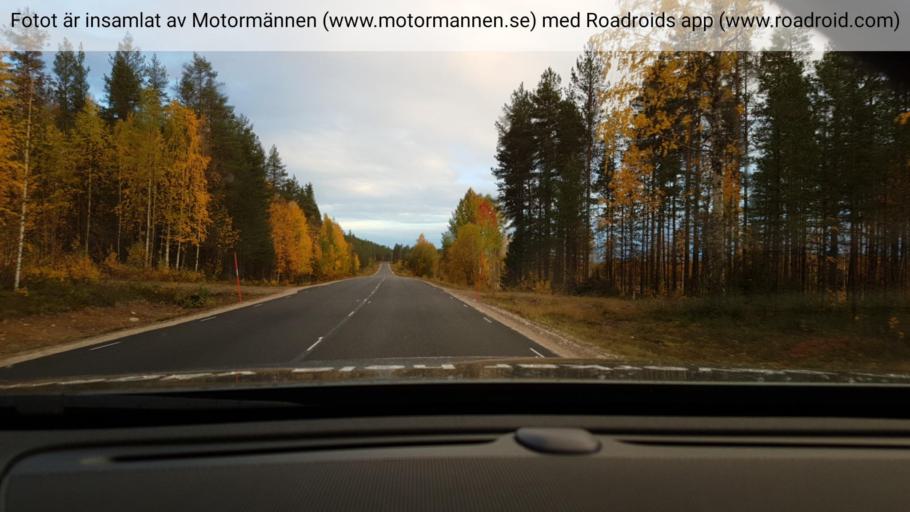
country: SE
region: Norrbotten
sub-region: Overkalix Kommun
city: OEverkalix
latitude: 66.4036
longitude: 22.8076
